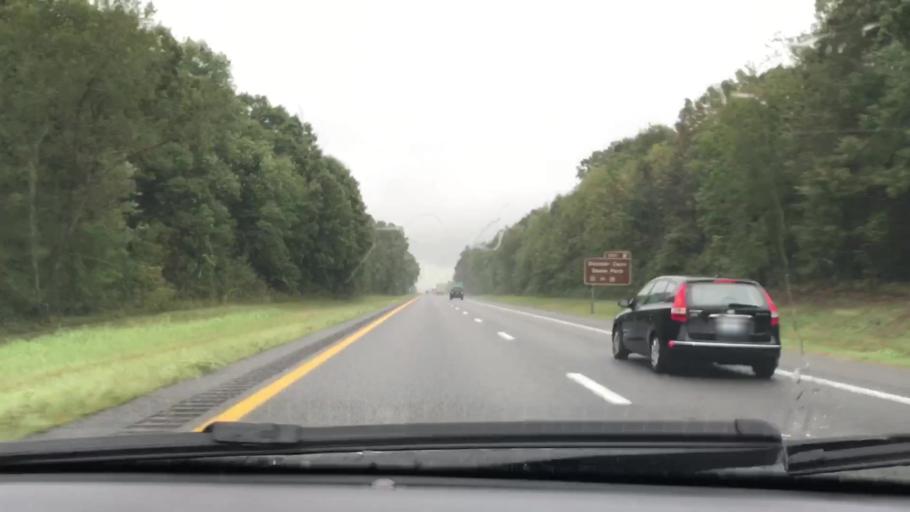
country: US
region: Tennessee
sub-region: Montgomery County
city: Clarksville
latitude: 36.5651
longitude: -87.2547
